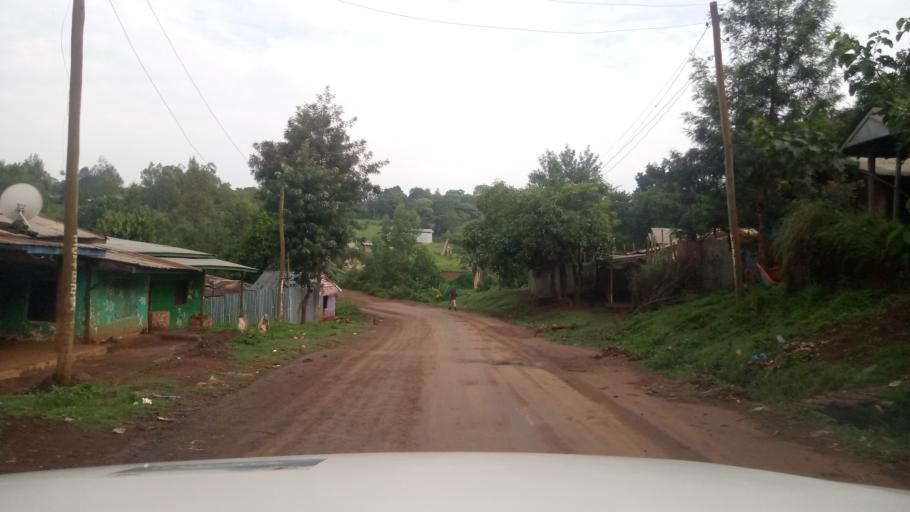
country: ET
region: Oromiya
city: Agaro
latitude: 7.8365
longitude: 36.6773
